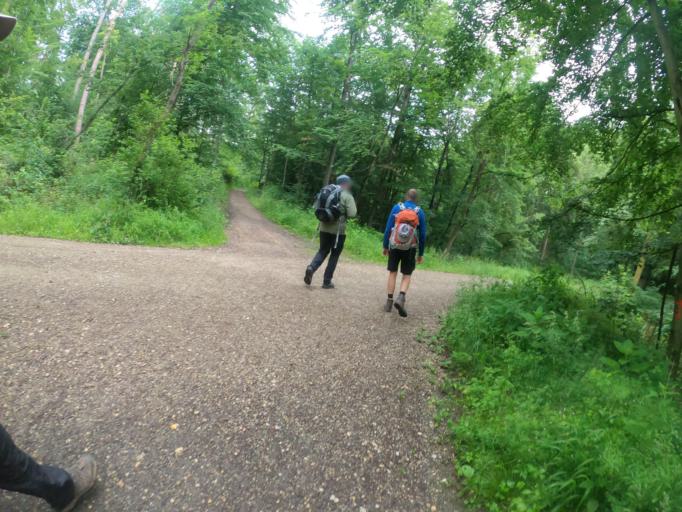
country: DE
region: Bavaria
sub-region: Upper Franconia
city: Memmelsdorf
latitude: 49.9266
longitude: 10.9713
